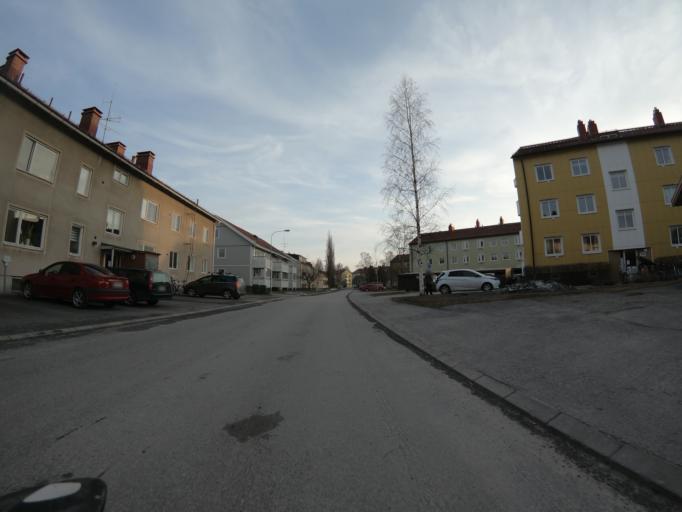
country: SE
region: Vaesterbotten
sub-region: Umea Kommun
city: Umea
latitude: 63.8351
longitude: 20.2732
